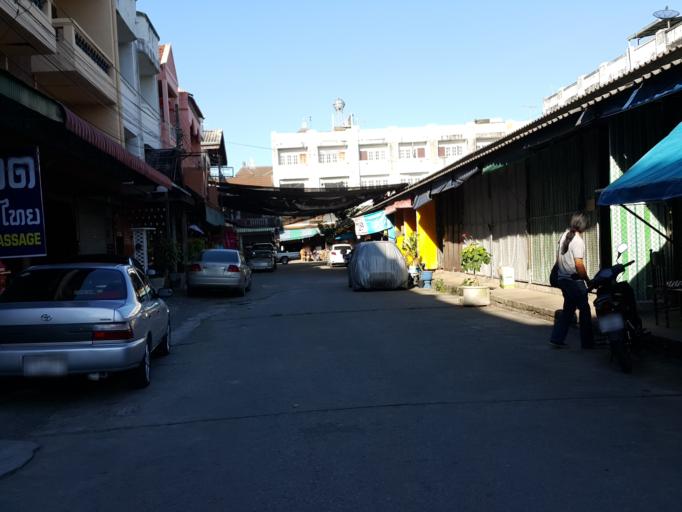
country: TH
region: Chiang Mai
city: San Kamphaeng
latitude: 18.7648
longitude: 99.0810
